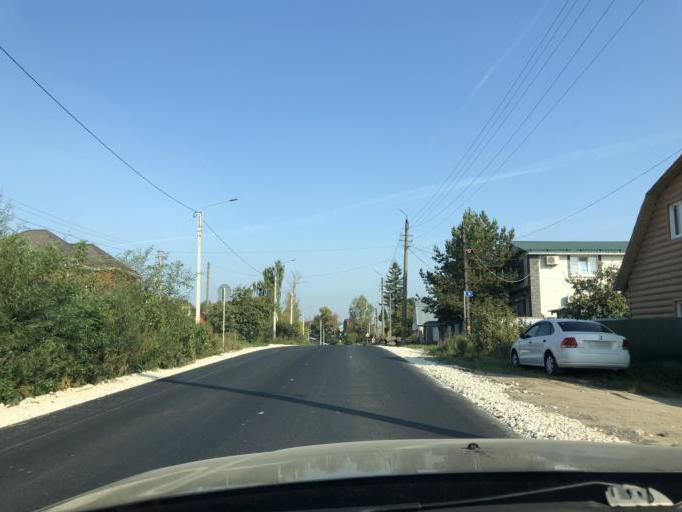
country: RU
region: Tula
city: Leninskiy
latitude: 54.2920
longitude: 37.4639
